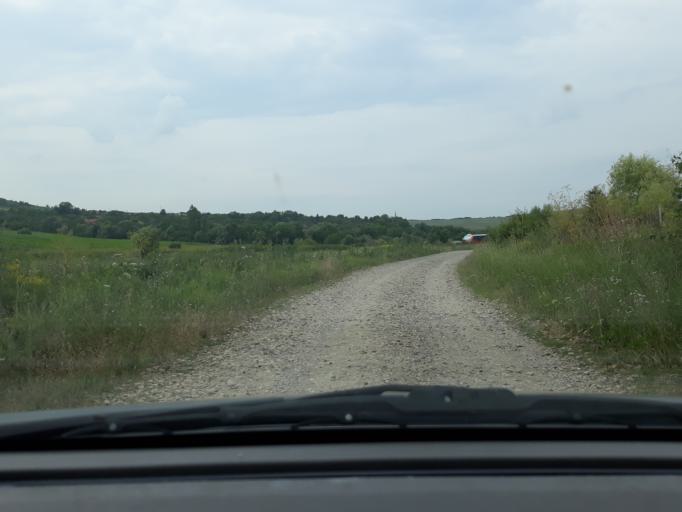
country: RO
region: Salaj
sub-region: Comuna Criseni
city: Criseni
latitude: 47.2650
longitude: 23.0669
